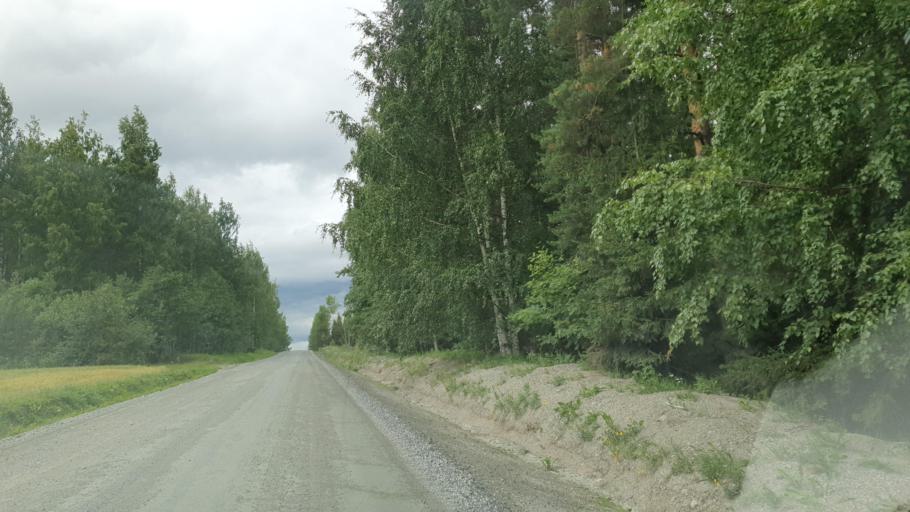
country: FI
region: Northern Savo
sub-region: Ylae-Savo
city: Iisalmi
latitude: 63.5226
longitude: 27.0953
